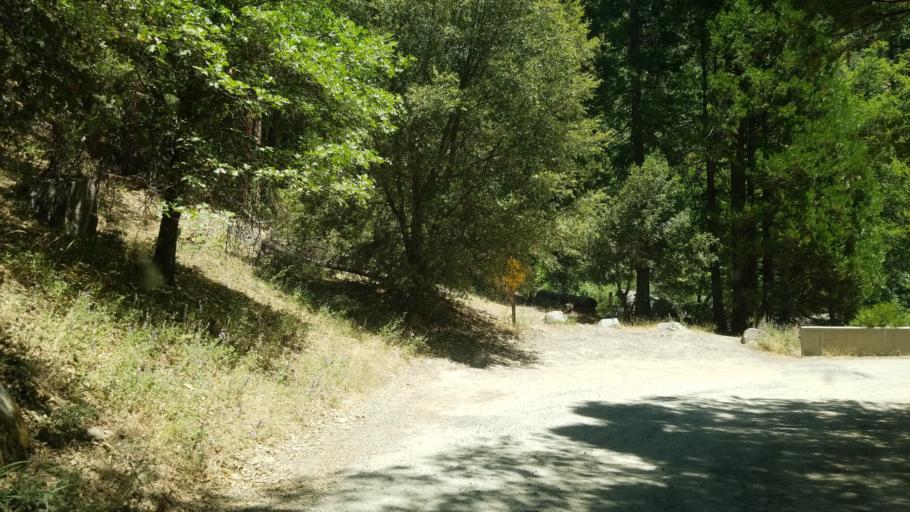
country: US
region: California
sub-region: Mariposa County
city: Yosemite Valley
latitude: 37.5489
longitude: -119.6329
